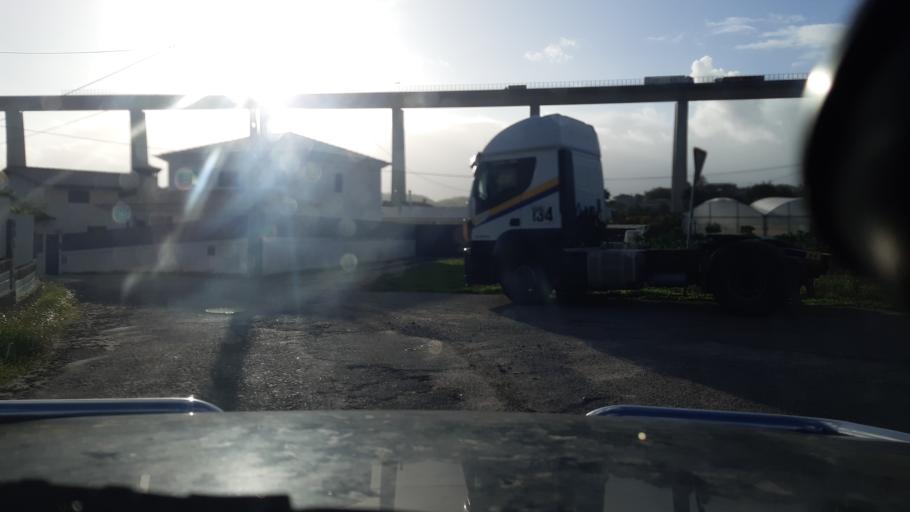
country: PT
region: Aveiro
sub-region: Agueda
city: Agueda
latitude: 40.5726
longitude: -8.4723
